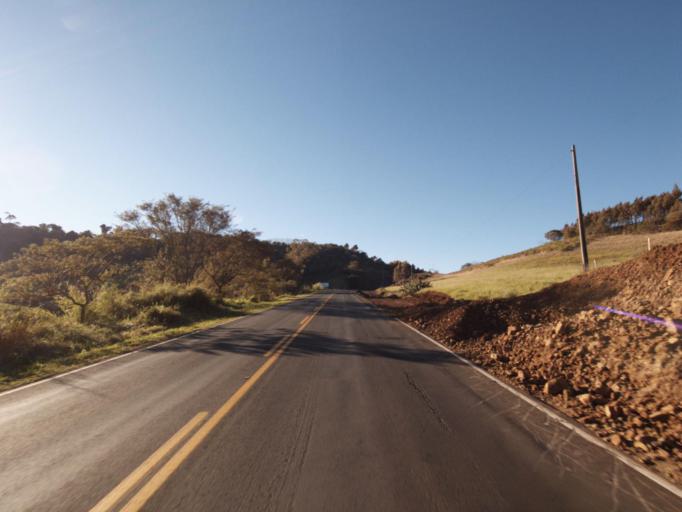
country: AR
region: Misiones
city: Bernardo de Irigoyen
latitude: -26.3567
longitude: -53.5395
